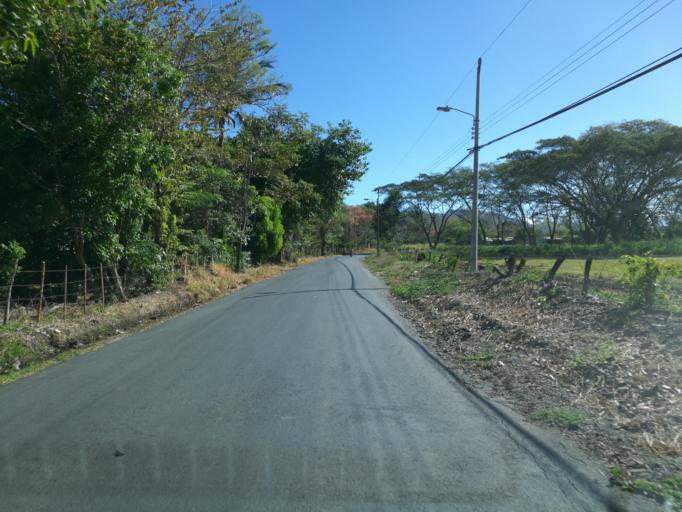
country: CR
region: Puntarenas
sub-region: Canton Central de Puntarenas
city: Puntarenas
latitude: 10.0911
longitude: -84.9578
